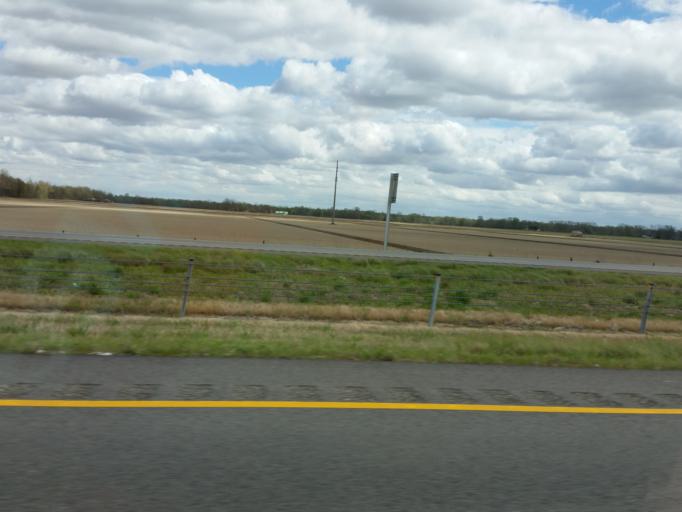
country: US
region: Arkansas
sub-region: Poinsett County
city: Marked Tree
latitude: 35.5562
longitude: -90.4969
